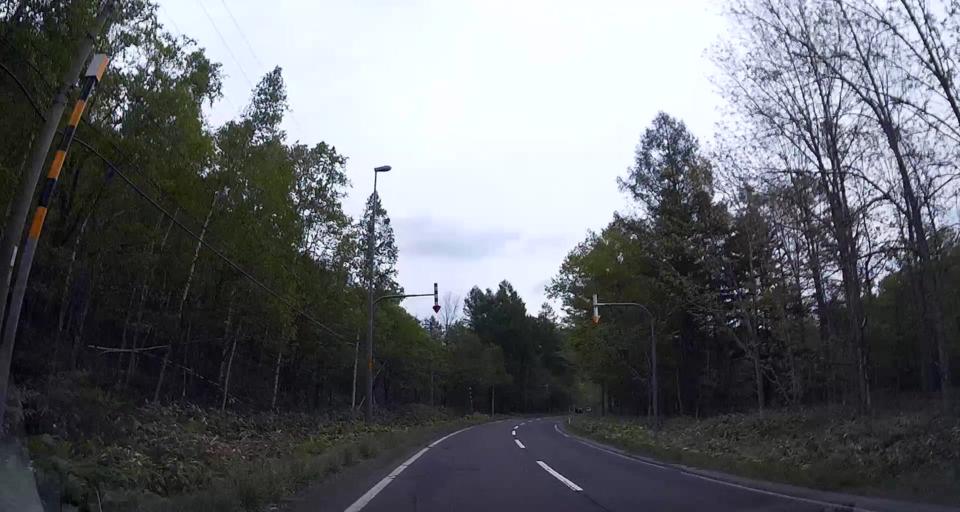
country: JP
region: Hokkaido
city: Shiraoi
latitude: 42.6880
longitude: 141.1031
